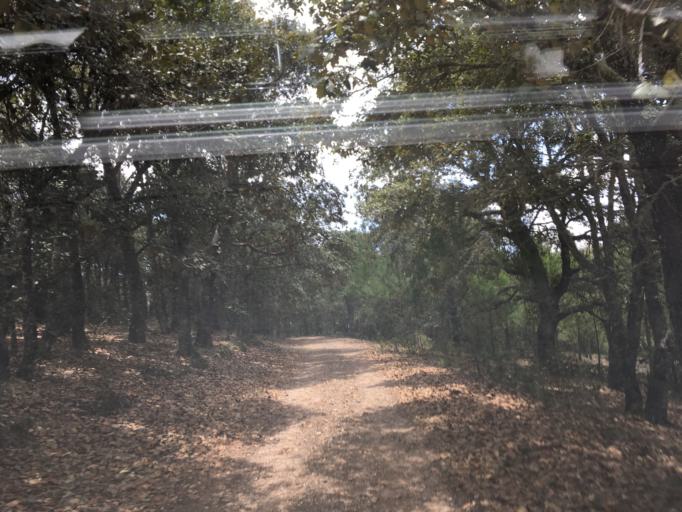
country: MX
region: Oaxaca
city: San Andres Sinaxtla
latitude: 17.6075
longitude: -97.2668
